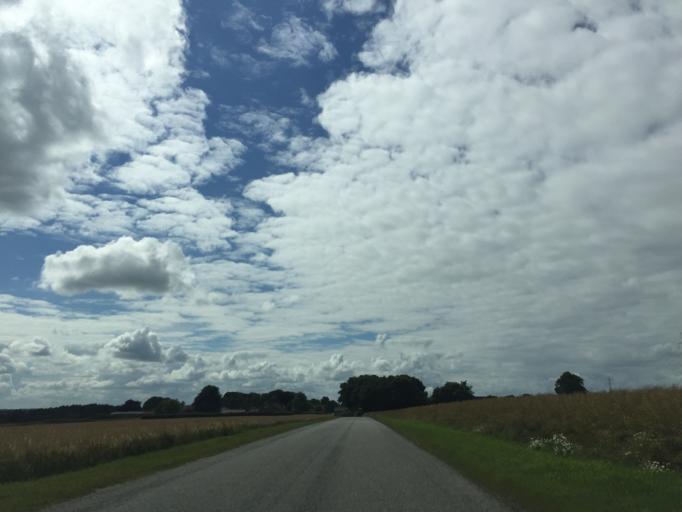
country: DK
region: Central Jutland
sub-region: Viborg Kommune
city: Bjerringbro
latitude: 56.3534
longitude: 9.6903
